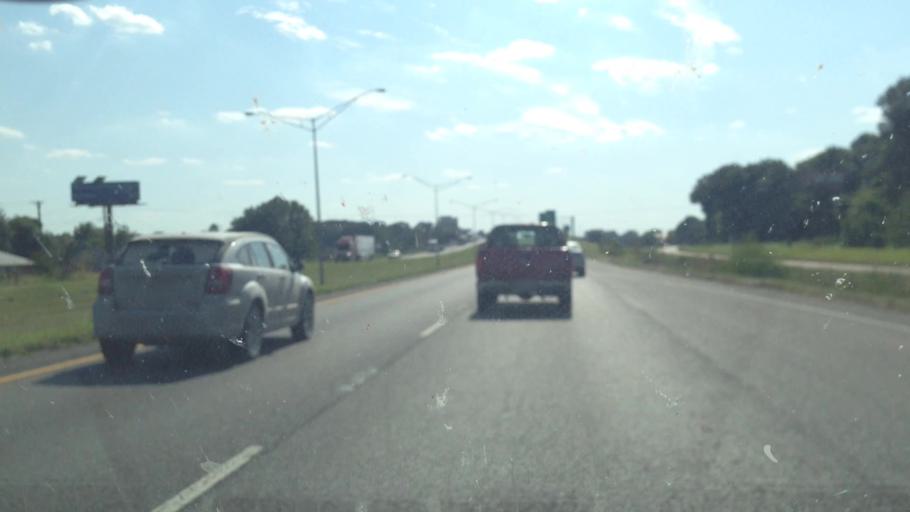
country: US
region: Louisiana
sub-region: Lafayette Parish
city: Lafayette
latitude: 30.2571
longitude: -92.0221
